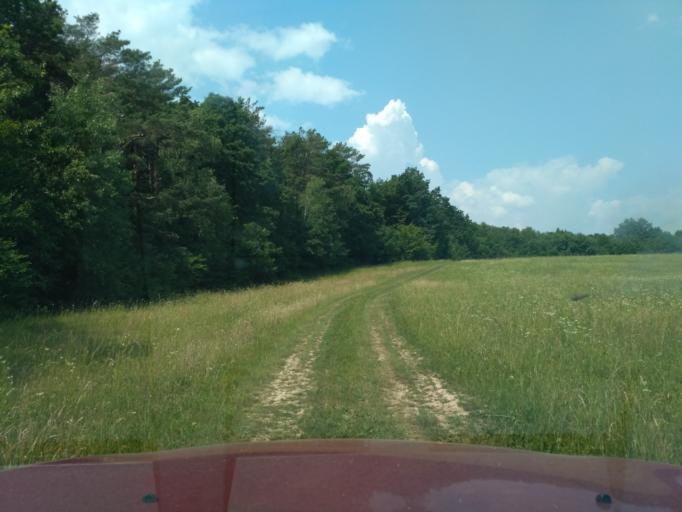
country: SK
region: Kosicky
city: Moldava nad Bodvou
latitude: 48.6253
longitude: 21.0449
